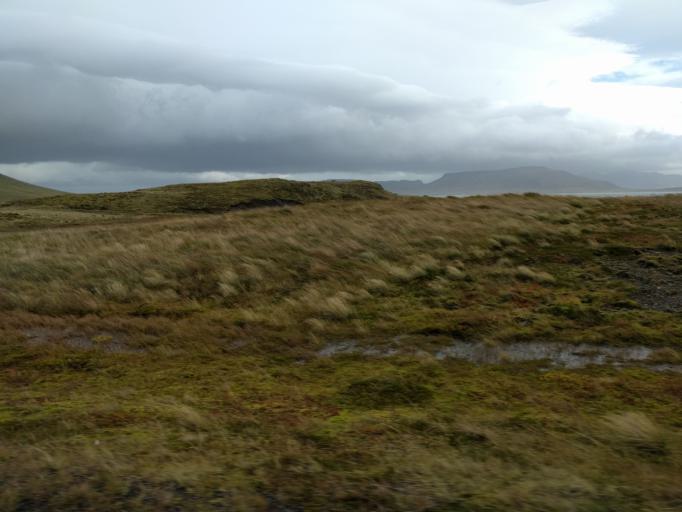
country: IS
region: West
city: Olafsvik
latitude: 64.9244
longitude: -23.2997
